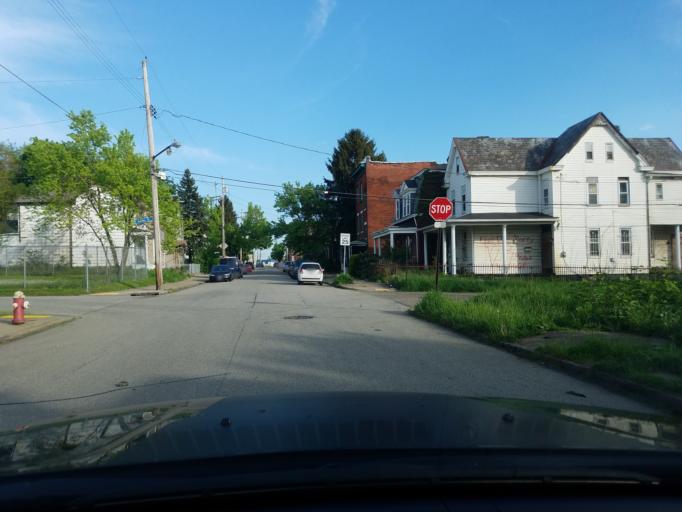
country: US
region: Pennsylvania
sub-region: Allegheny County
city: Aspinwall
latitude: 40.4630
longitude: -79.9153
